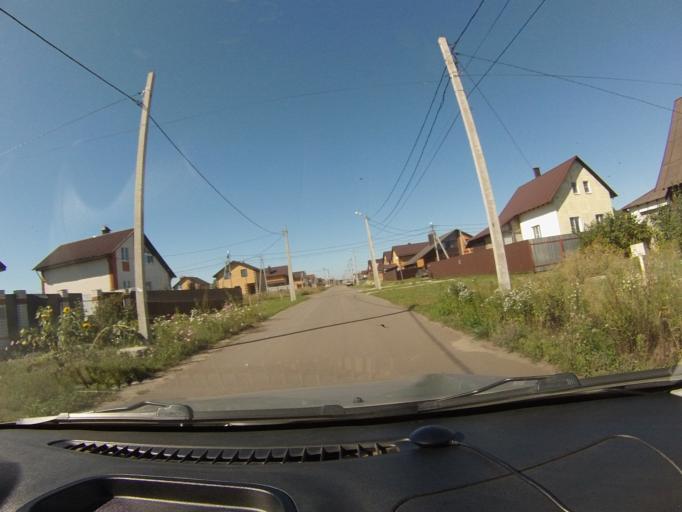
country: RU
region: Tambov
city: Tambov
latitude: 52.7739
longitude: 41.3746
